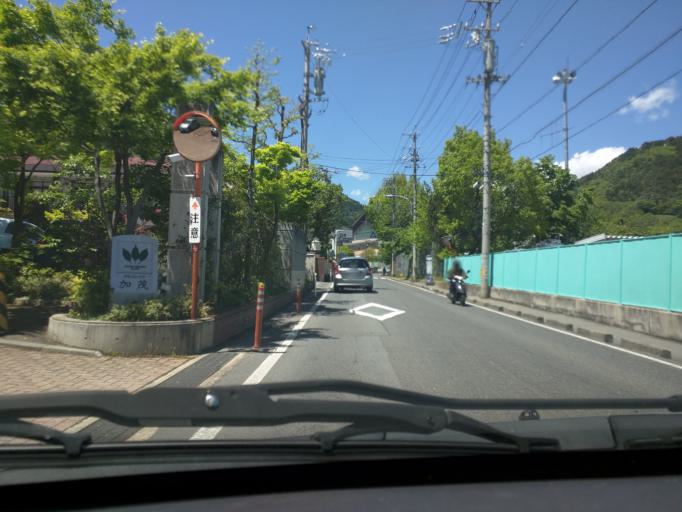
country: JP
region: Nagano
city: Nagano-shi
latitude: 36.6570
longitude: 138.1766
